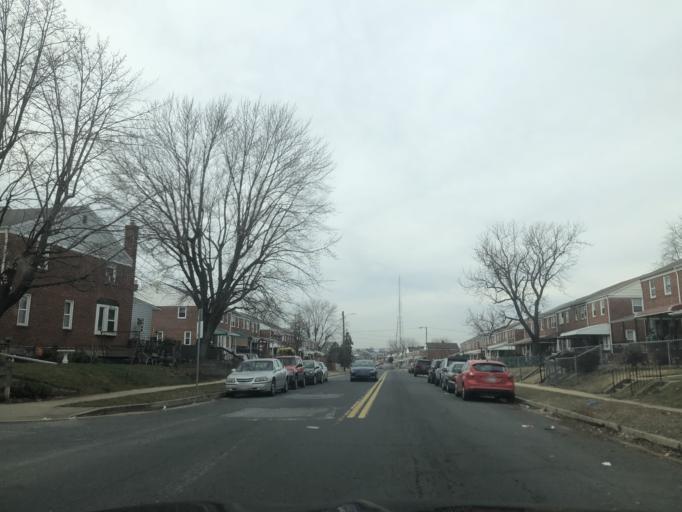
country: US
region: Maryland
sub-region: Baltimore County
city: Dundalk
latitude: 39.2644
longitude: -76.4944
